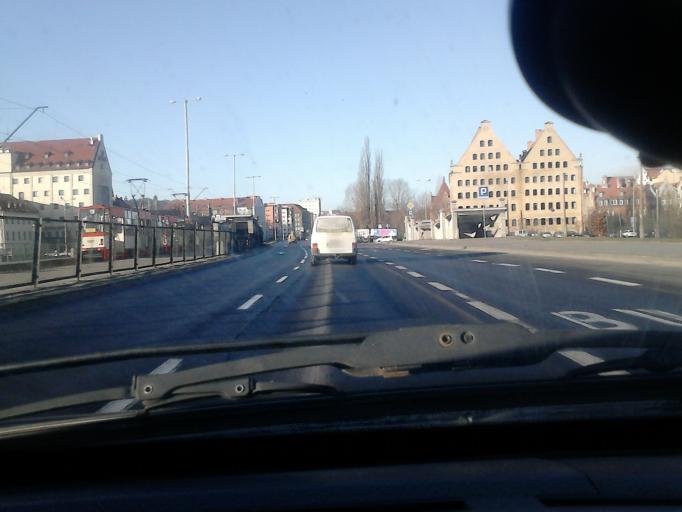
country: PL
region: Pomeranian Voivodeship
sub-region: Gdansk
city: Gdansk
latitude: 54.3454
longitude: 18.6581
